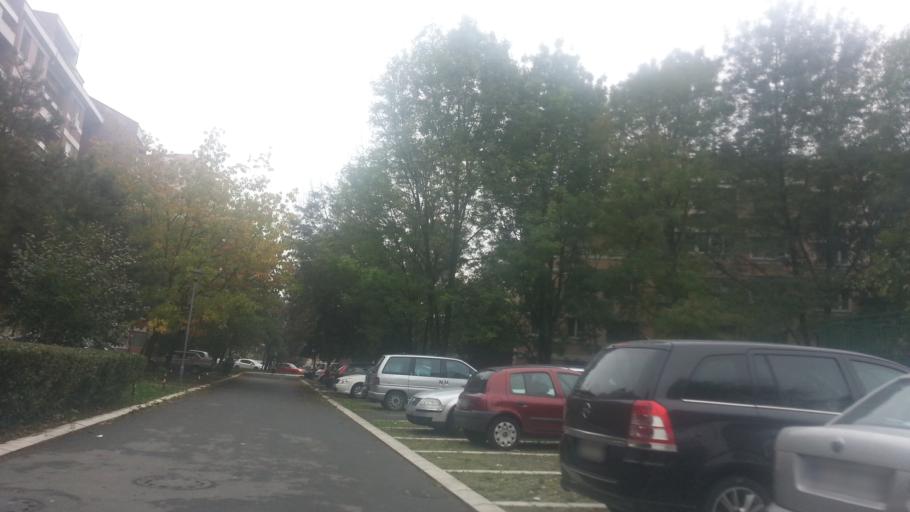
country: RS
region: Central Serbia
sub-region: Belgrade
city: Zemun
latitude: 44.8473
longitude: 20.3822
